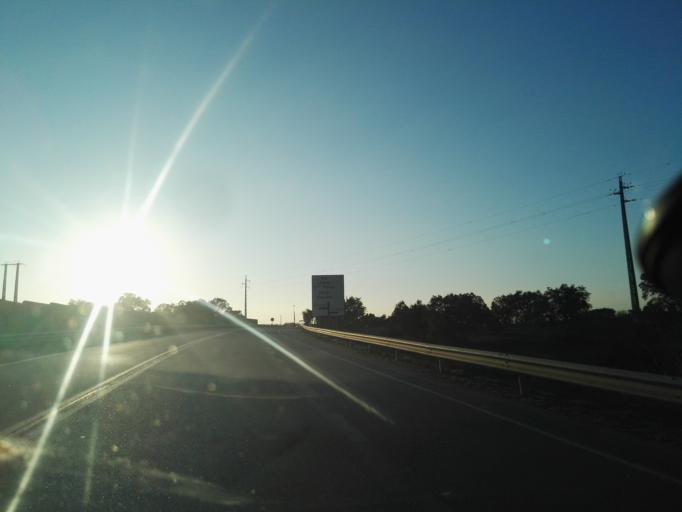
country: PT
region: Evora
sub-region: Montemor-O-Novo
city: Montemor-o-Novo
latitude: 38.6477
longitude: -8.2542
